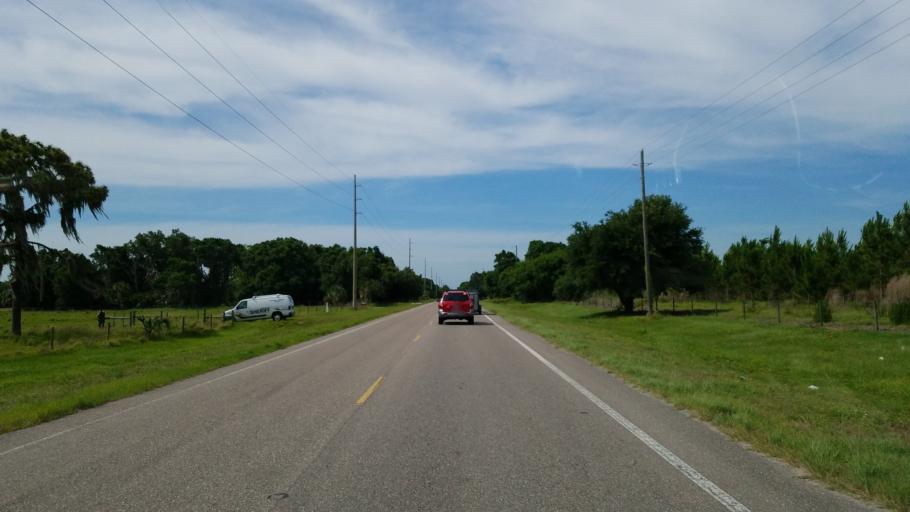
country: US
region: Florida
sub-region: Hillsborough County
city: Balm
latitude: 27.6736
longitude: -82.1462
